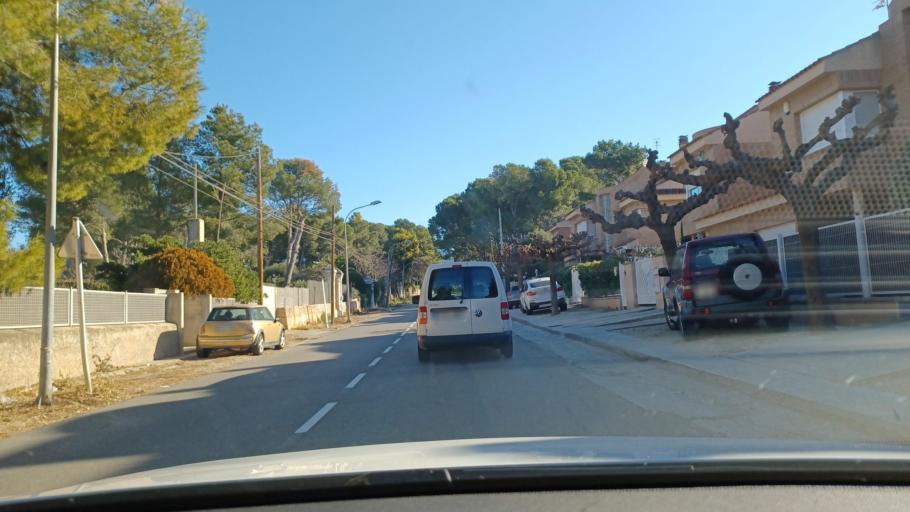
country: ES
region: Catalonia
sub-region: Provincia de Tarragona
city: Tortosa
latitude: 40.8125
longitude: 0.5304
